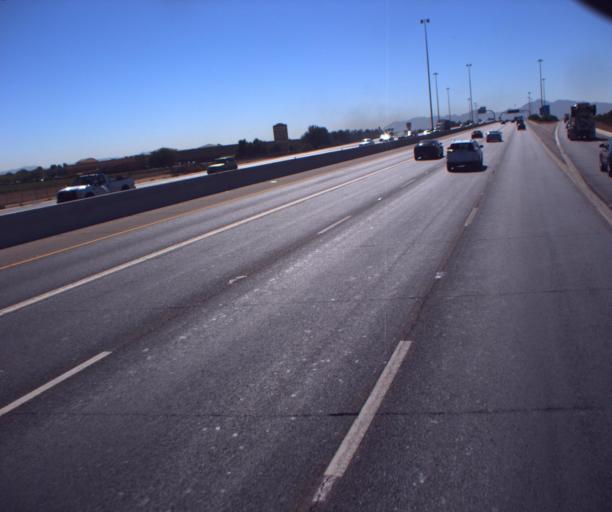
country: US
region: Arizona
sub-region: Maricopa County
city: Tolleson
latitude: 33.5141
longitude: -112.2693
